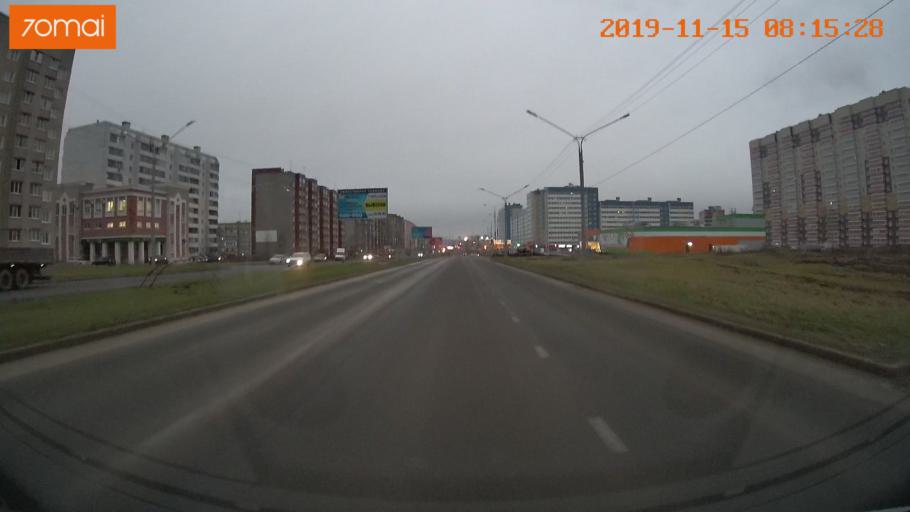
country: RU
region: Vologda
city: Cherepovets
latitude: 59.0826
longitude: 37.9221
